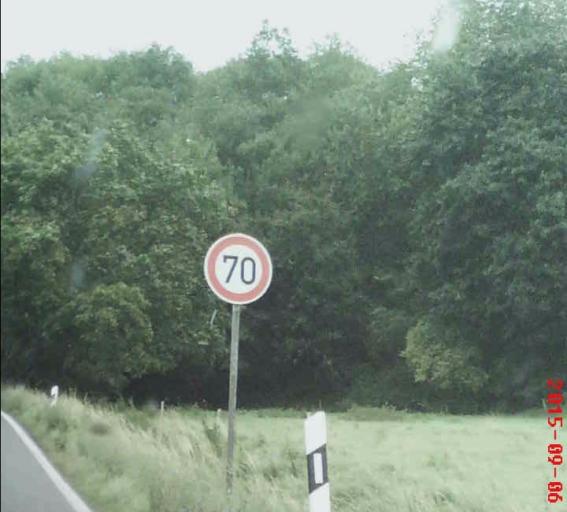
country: DE
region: Thuringia
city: Weissenborn-Luderode
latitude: 51.5268
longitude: 10.4417
